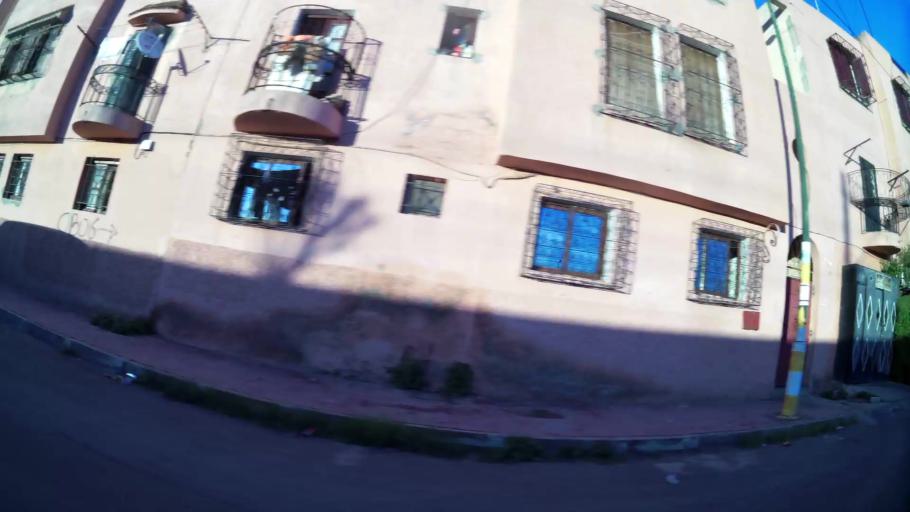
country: MA
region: Marrakech-Tensift-Al Haouz
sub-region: Marrakech
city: Marrakesh
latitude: 31.6387
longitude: -8.0393
